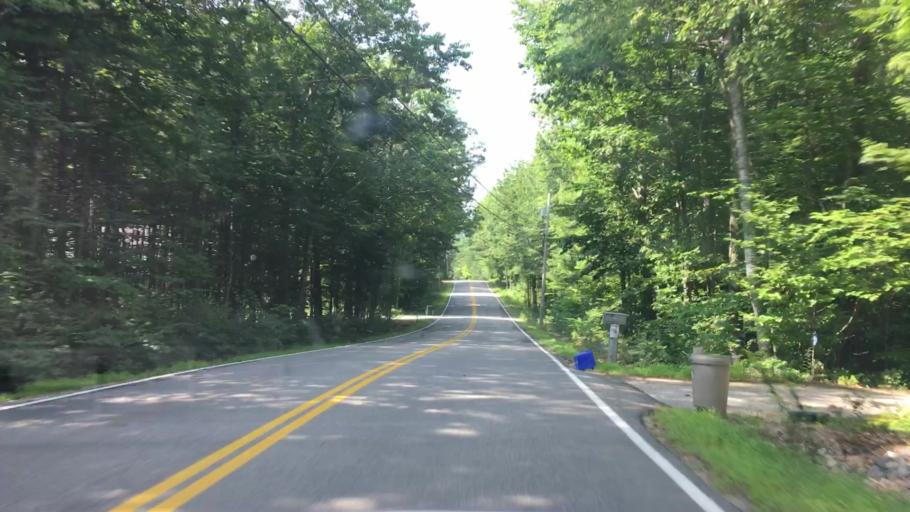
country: US
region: Maine
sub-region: Cumberland County
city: Raymond
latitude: 43.9624
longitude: -70.4154
